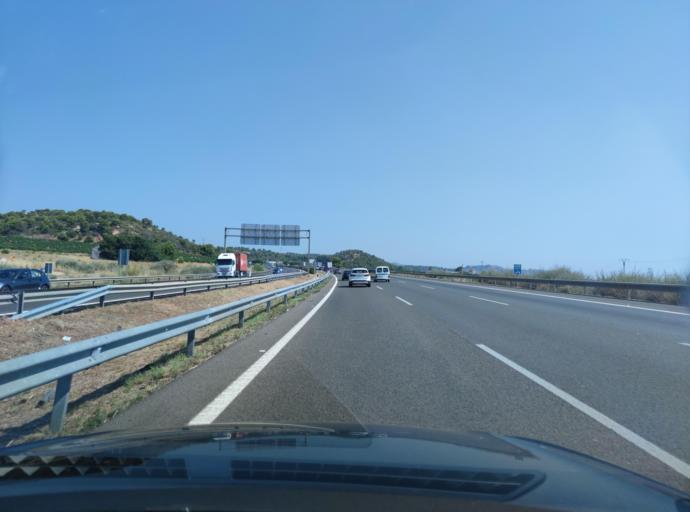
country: ES
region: Valencia
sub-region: Provincia de Valencia
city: Pucol
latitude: 39.6428
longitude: -0.3003
